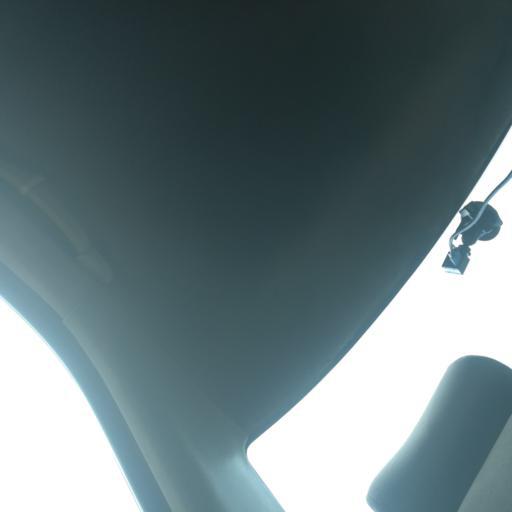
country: NG
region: Lagos
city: Ejirin
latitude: 6.6477
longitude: 3.7169
